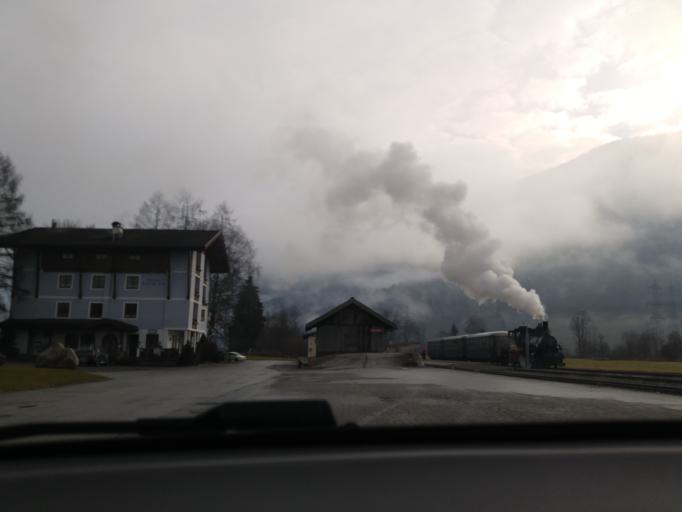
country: AT
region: Salzburg
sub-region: Politischer Bezirk Zell am See
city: Uttendorf
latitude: 47.2816
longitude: 12.5732
